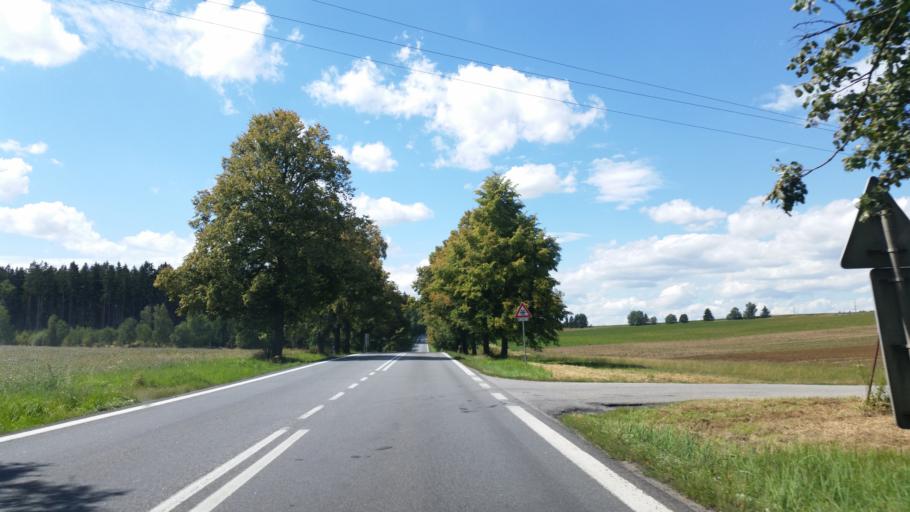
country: CZ
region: Vysocina
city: Cernovice
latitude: 49.4275
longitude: 14.9275
